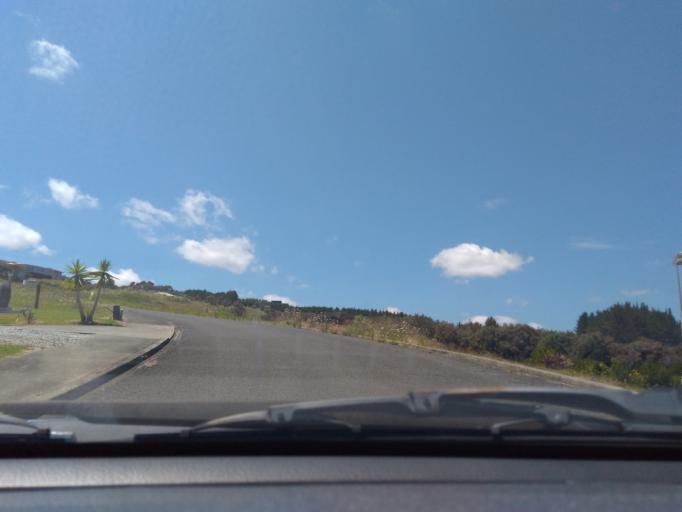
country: NZ
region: Northland
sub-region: Far North District
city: Taipa
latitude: -34.9949
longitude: 173.5052
